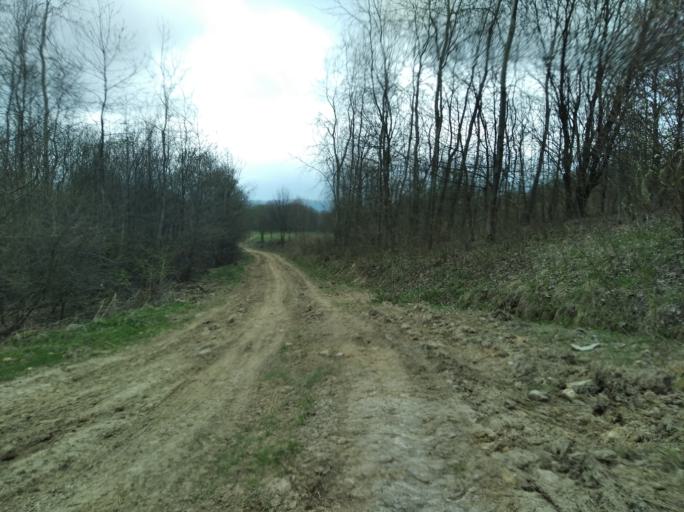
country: PL
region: Subcarpathian Voivodeship
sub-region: Powiat strzyzowski
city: Jawornik
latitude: 49.8181
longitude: 21.9018
